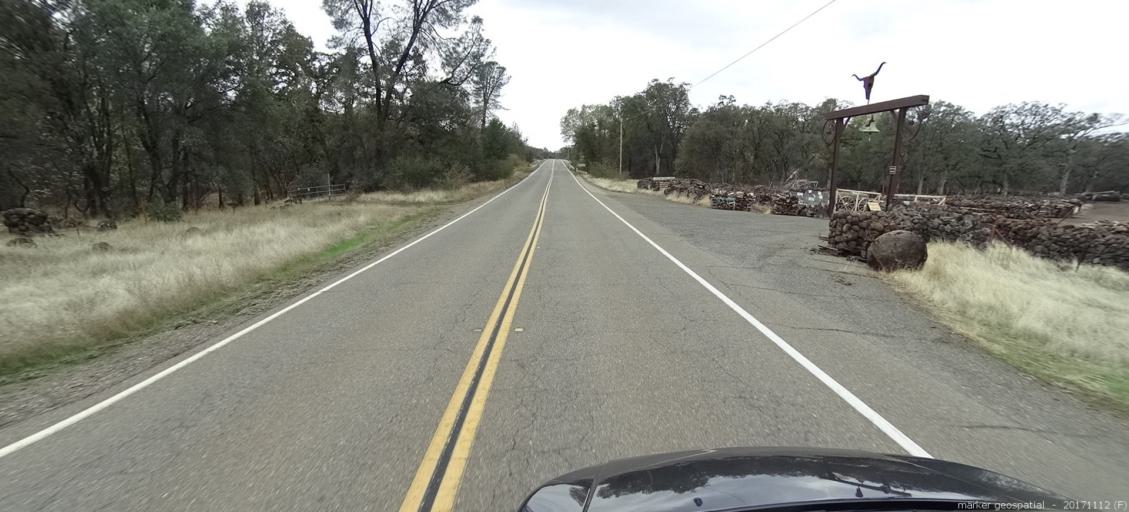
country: US
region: California
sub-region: Shasta County
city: Shingletown
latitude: 40.4886
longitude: -122.0714
